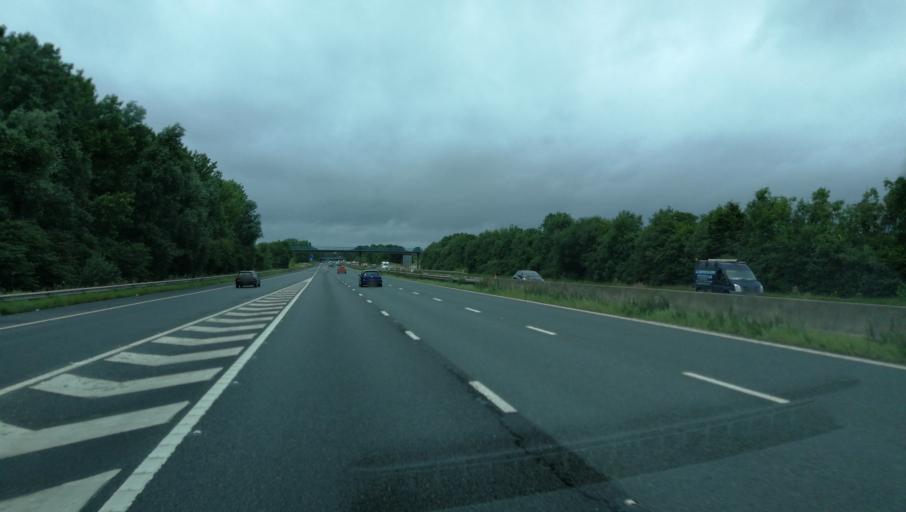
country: GB
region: England
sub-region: Borough of Wigan
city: Tyldesley
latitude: 53.5457
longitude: -2.4537
